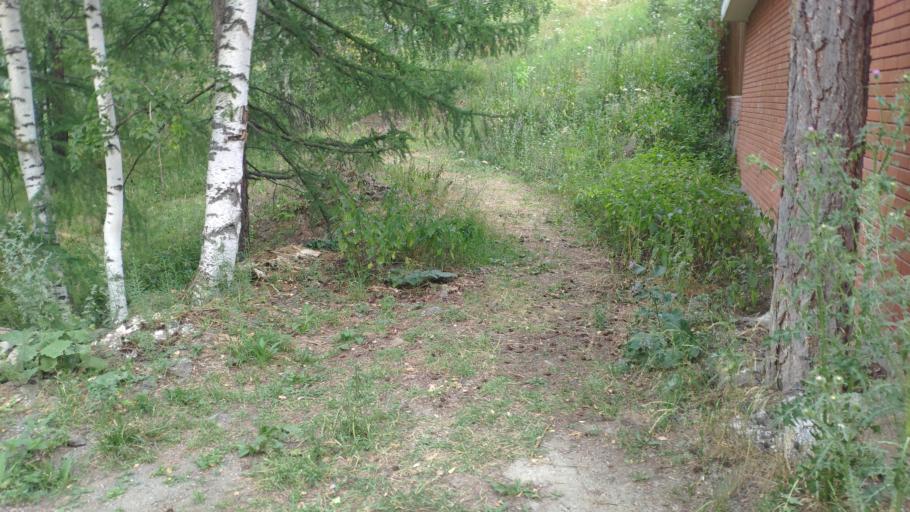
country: RU
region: Bashkortostan
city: Abzakovo
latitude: 53.8040
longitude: 58.6440
